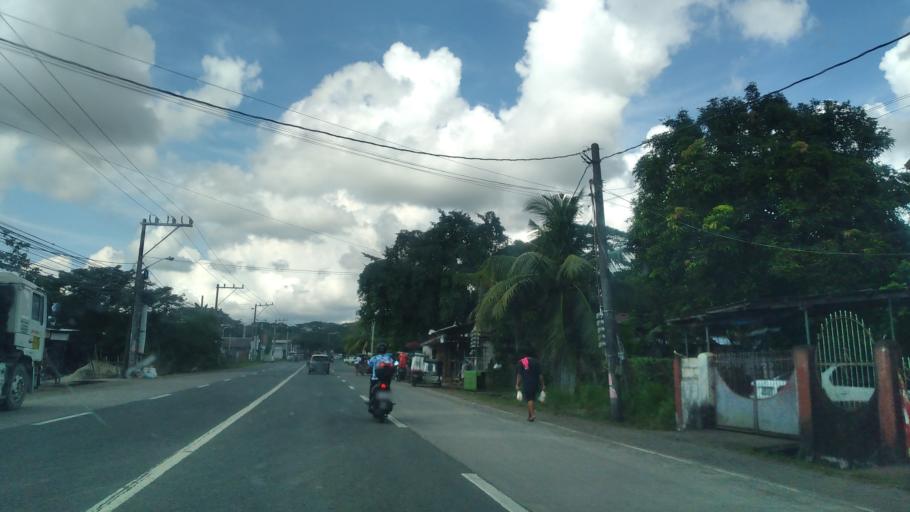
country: PH
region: Calabarzon
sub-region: Province of Quezon
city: Isabang
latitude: 13.9534
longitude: 121.5750
